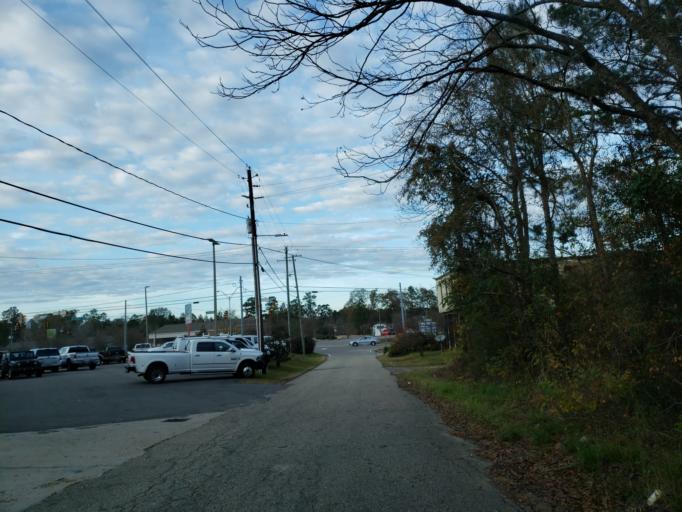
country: US
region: Mississippi
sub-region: Forrest County
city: Hattiesburg
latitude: 31.3034
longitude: -89.3200
